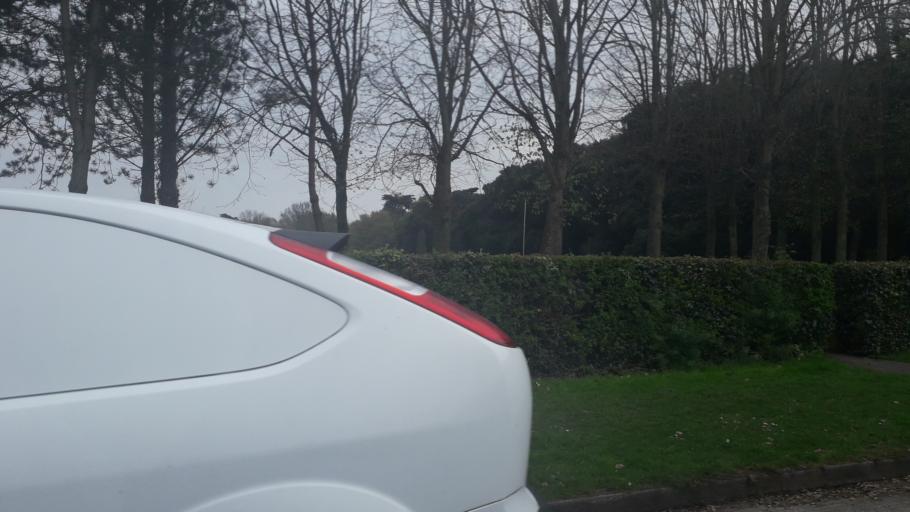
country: IE
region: Leinster
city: Dollymount
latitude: 53.3752
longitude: -6.1739
